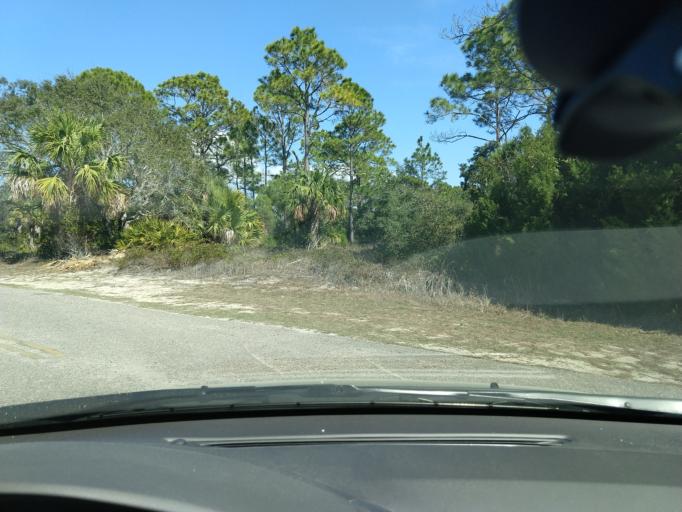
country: US
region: Florida
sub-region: Gulf County
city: Port Saint Joe
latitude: 29.6786
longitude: -85.2346
